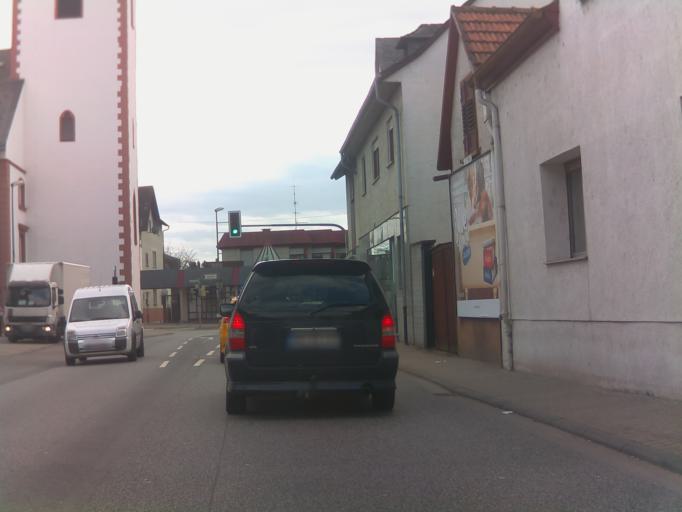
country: DE
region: Hesse
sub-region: Regierungsbezirk Darmstadt
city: Gross-Gerau
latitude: 49.8780
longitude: 8.4817
